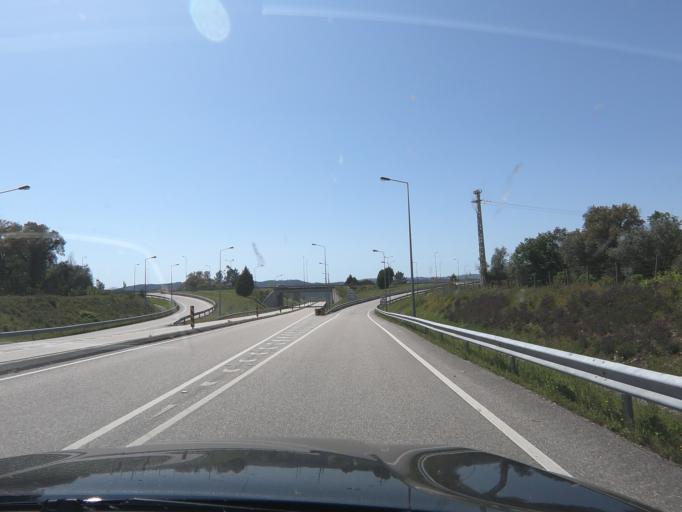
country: PT
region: Coimbra
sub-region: Lousa
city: Lousa
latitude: 40.1283
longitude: -8.2464
